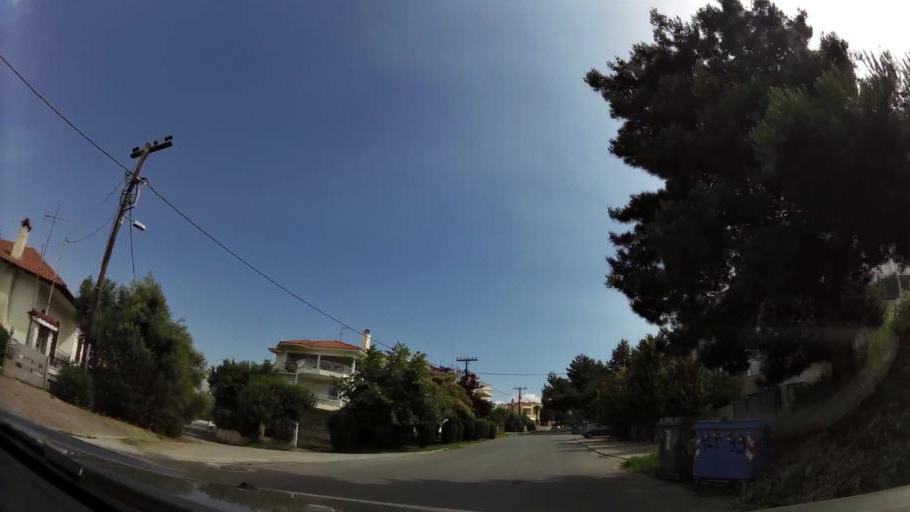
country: GR
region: Central Macedonia
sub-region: Nomos Thessalonikis
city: Panorama
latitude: 40.5799
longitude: 23.0068
